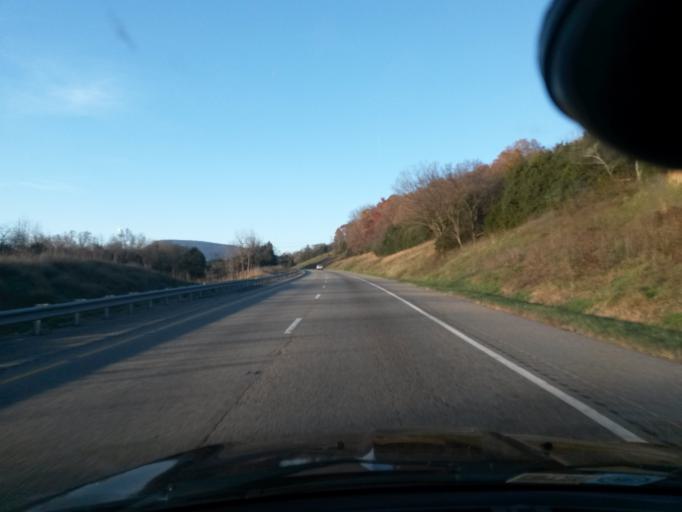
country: US
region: Virginia
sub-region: Rockbridge County
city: East Lexington
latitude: 37.8299
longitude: -79.4432
